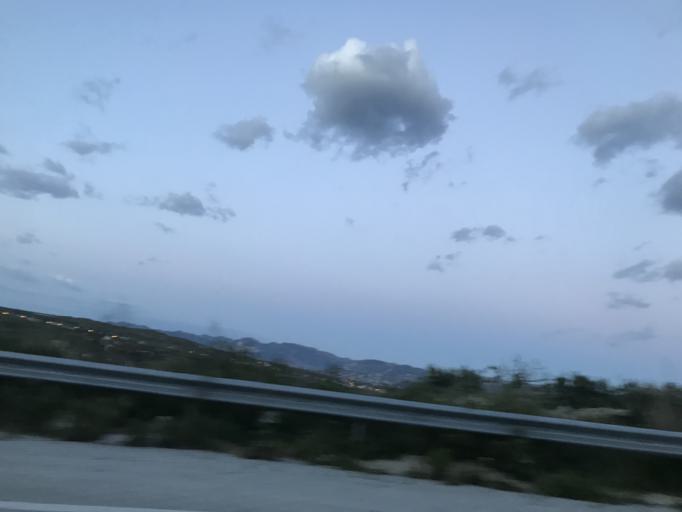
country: TR
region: Hatay
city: Uzunbag
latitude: 36.1294
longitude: 36.0420
